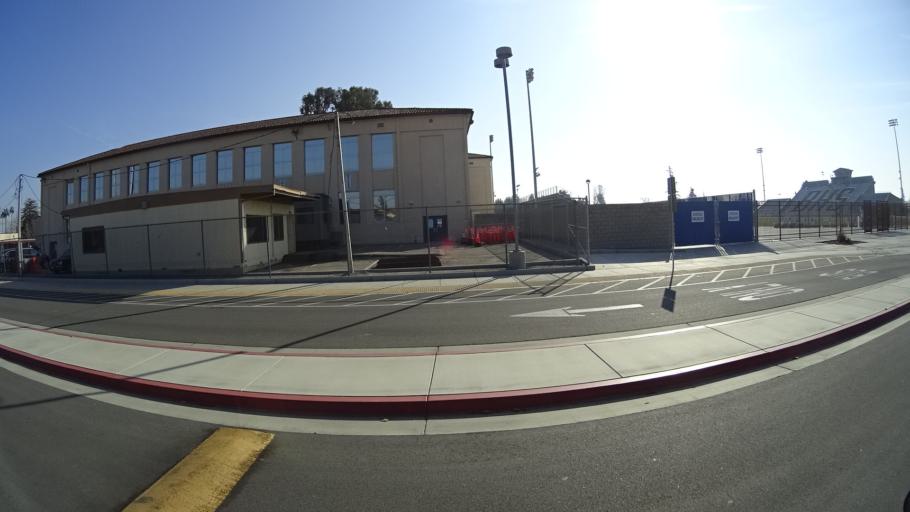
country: US
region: California
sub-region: Kern County
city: Bakersfield
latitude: 35.3705
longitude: -119.0253
